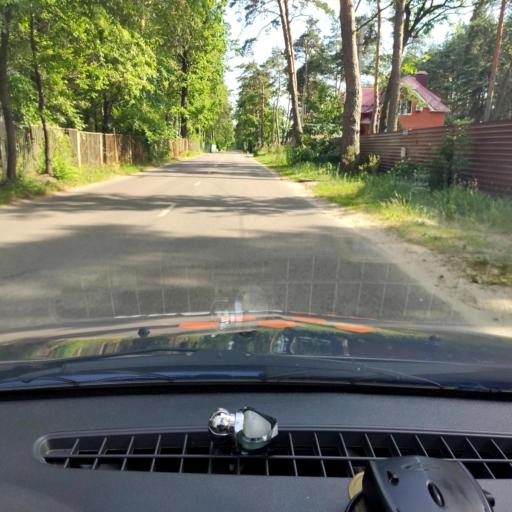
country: RU
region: Voronezj
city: Somovo
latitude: 51.7545
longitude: 39.3660
